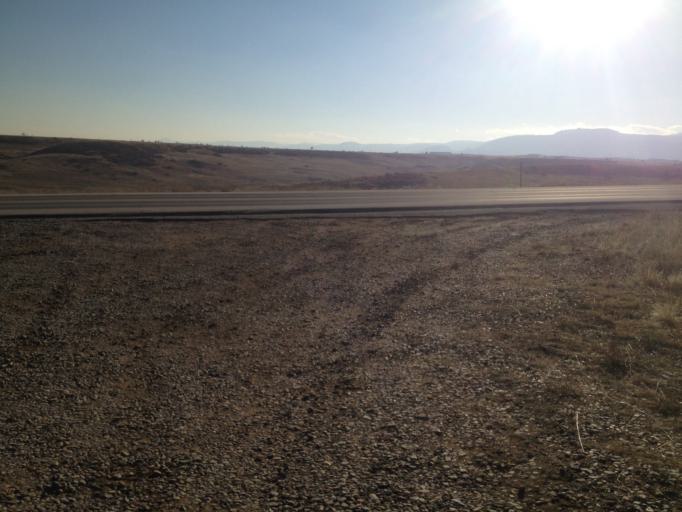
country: US
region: Colorado
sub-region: Boulder County
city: Superior
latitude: 39.9140
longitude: -105.2064
